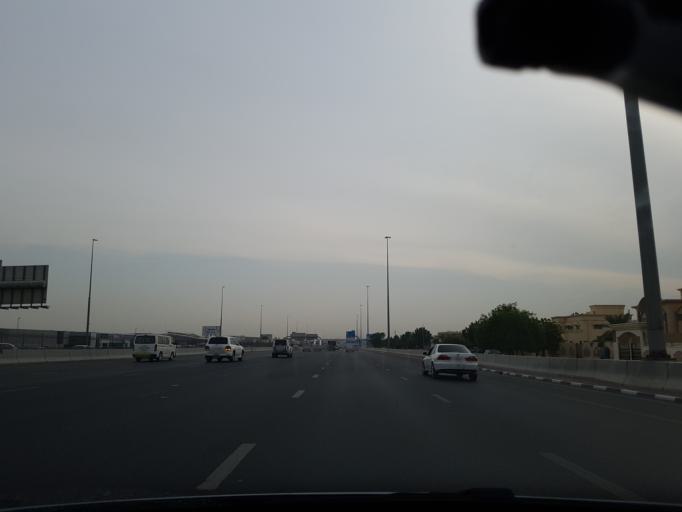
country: AE
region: Ash Shariqah
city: Sharjah
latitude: 25.3533
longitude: 55.4786
